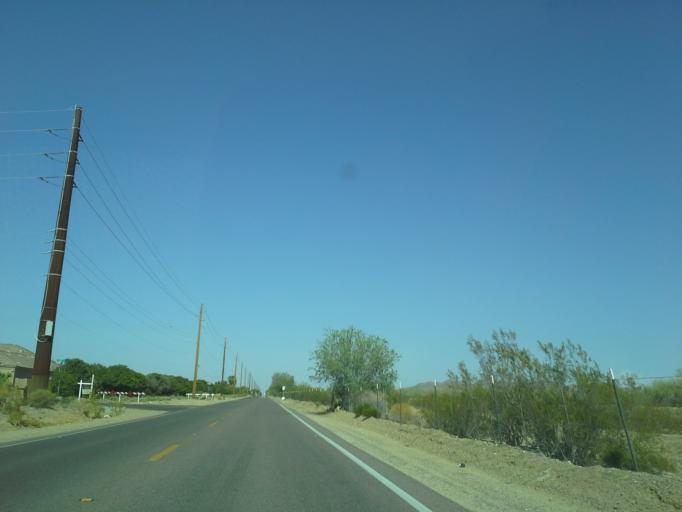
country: US
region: Arizona
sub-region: Maricopa County
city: Queen Creek
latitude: 33.2046
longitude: -111.7124
